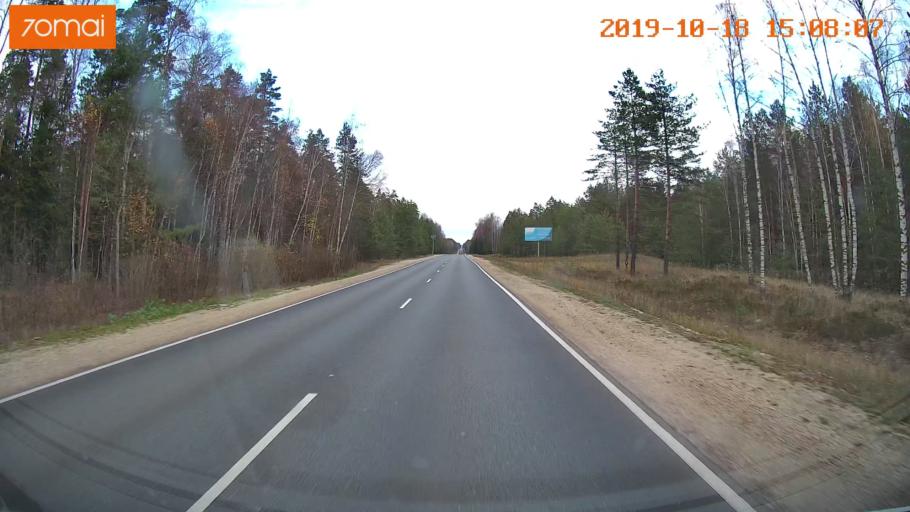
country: RU
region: Vladimir
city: Gus'-Khrustal'nyy
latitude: 55.5480
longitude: 40.6072
